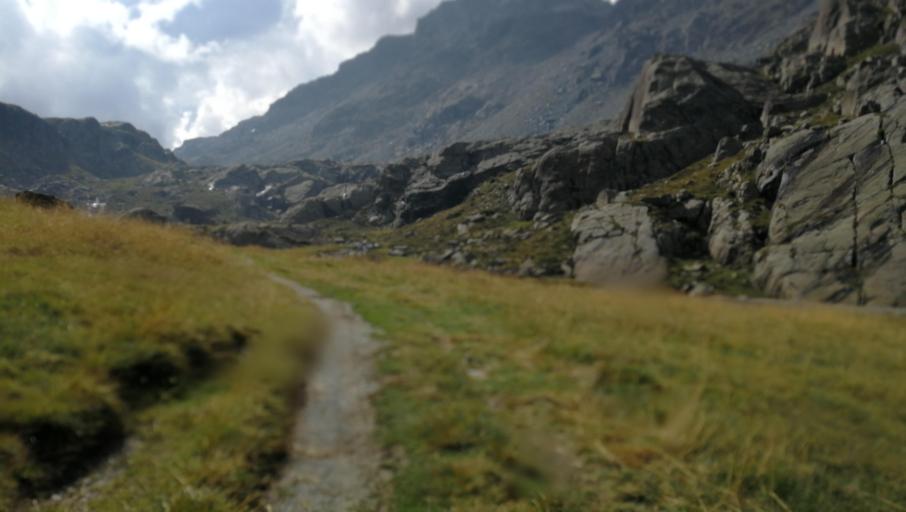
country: CH
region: Grisons
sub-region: Bernina District
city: Poschiavo
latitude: 46.3190
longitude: 9.9648
